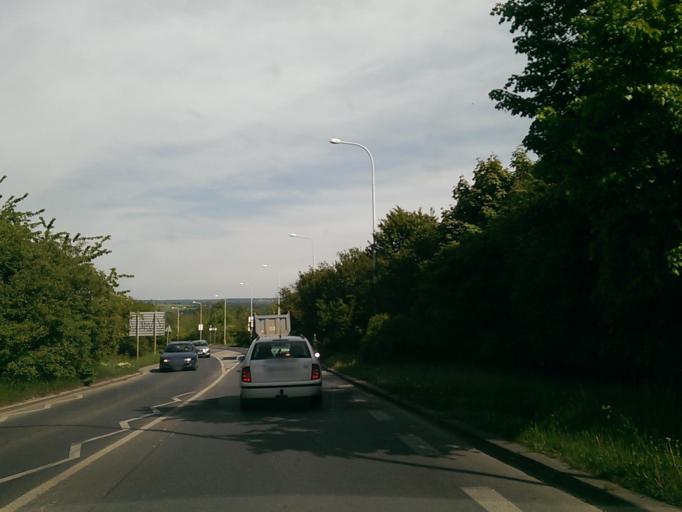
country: CZ
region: Central Bohemia
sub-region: Okres Praha-Zapad
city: Pruhonice
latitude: 50.0337
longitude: 14.5385
